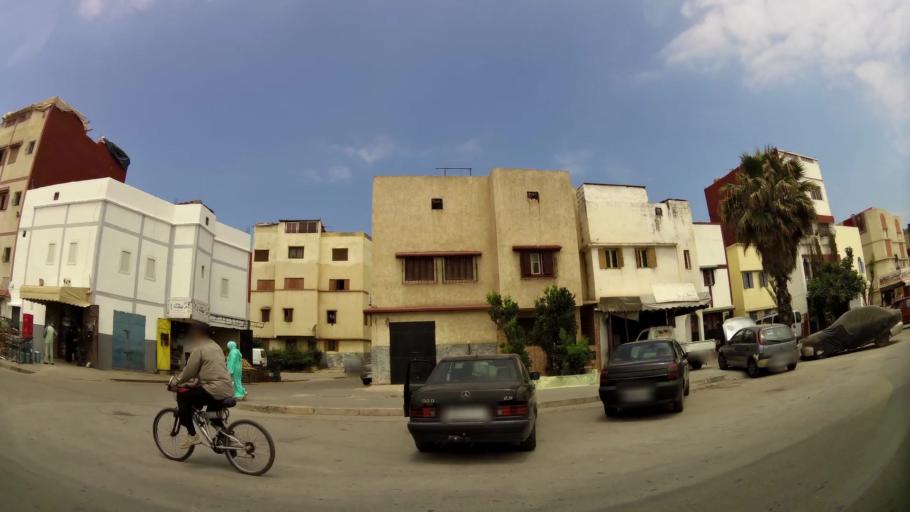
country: MA
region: Rabat-Sale-Zemmour-Zaer
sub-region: Rabat
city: Rabat
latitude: 33.9859
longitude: -6.8864
